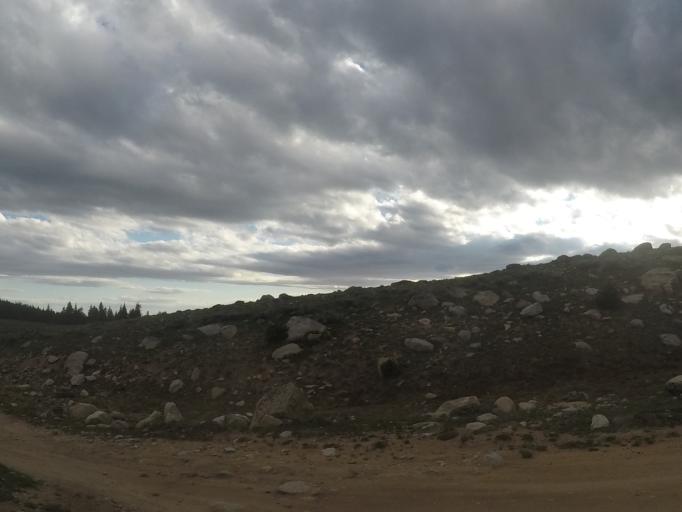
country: US
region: Wyoming
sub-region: Sheridan County
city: Sheridan
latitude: 44.5045
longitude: -107.4311
